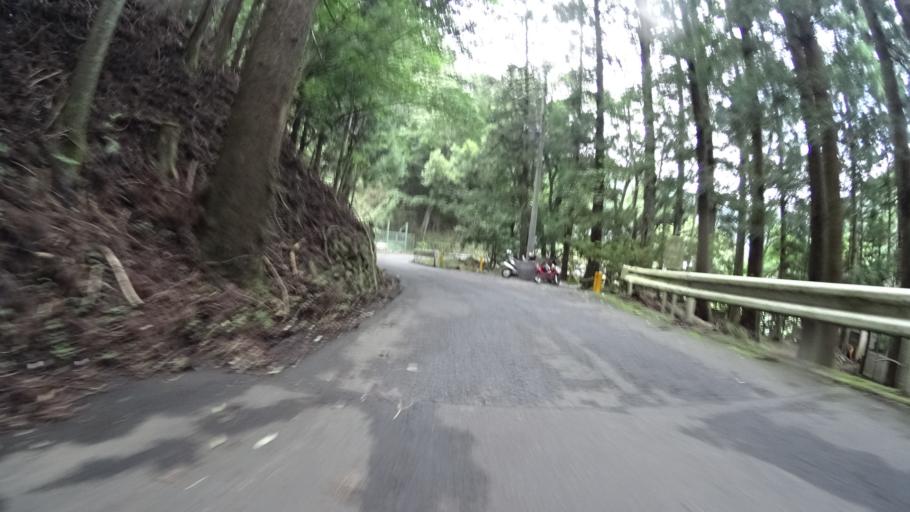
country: JP
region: Kanagawa
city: Hadano
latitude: 35.4921
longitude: 139.2198
